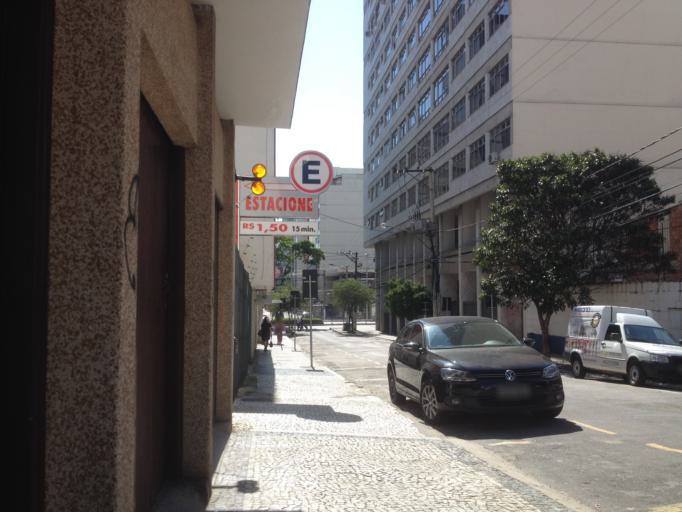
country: BR
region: Minas Gerais
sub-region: Juiz De Fora
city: Juiz de Fora
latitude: -21.7653
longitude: -43.3496
